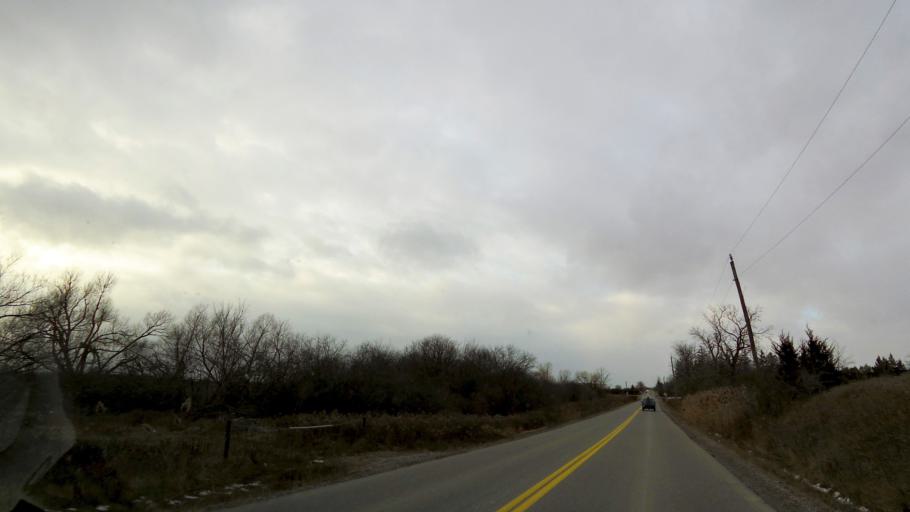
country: CA
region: Ontario
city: Brampton
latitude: 43.8189
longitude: -79.7028
